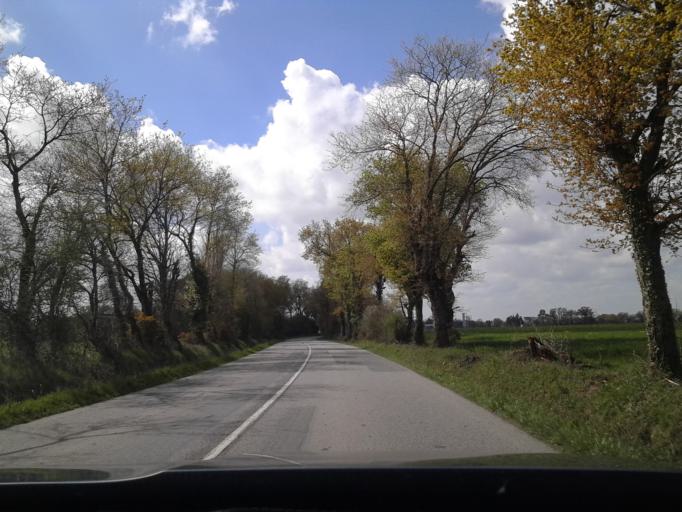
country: FR
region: Brittany
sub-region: Departement d'Ille-et-Vilaine
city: Grand-Fougeray
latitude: 47.7346
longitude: -1.7221
